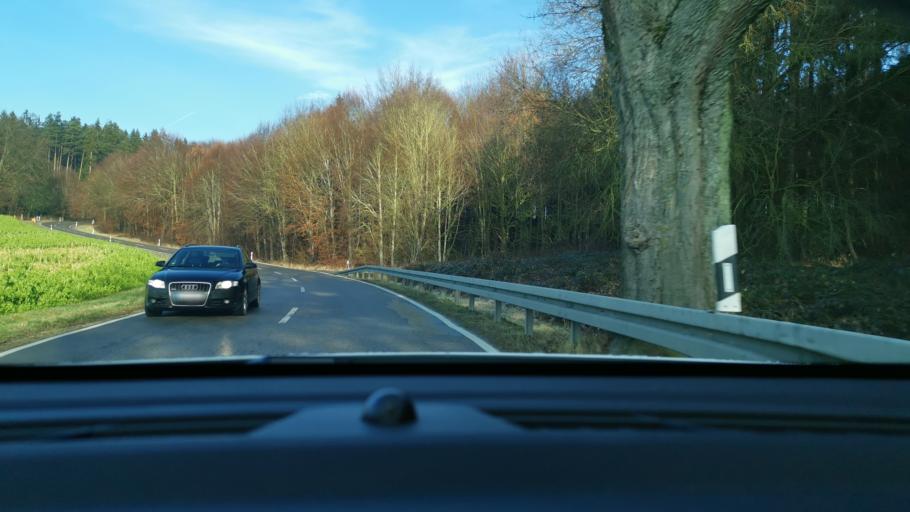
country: DE
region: Bavaria
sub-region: Swabia
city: Petersdorf
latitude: 48.5421
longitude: 11.0013
